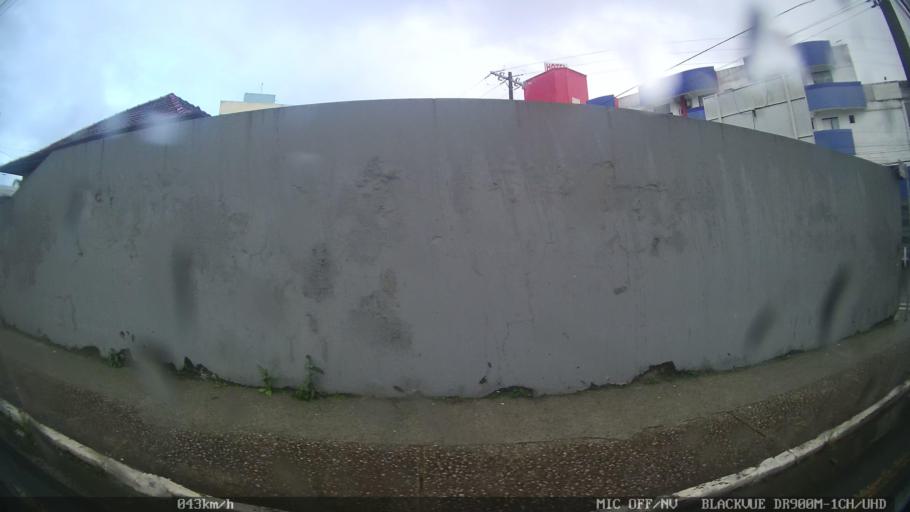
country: BR
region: Santa Catarina
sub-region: Sao Jose
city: Campinas
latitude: -27.6066
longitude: -48.6262
